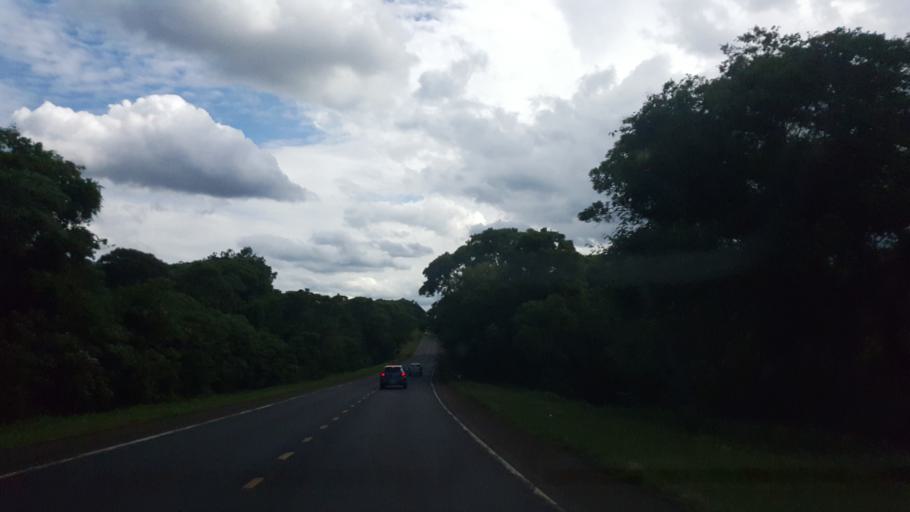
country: AR
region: Misiones
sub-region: Departamento de Iguazu
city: Puerto Iguazu
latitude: -25.7042
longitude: -54.5150
